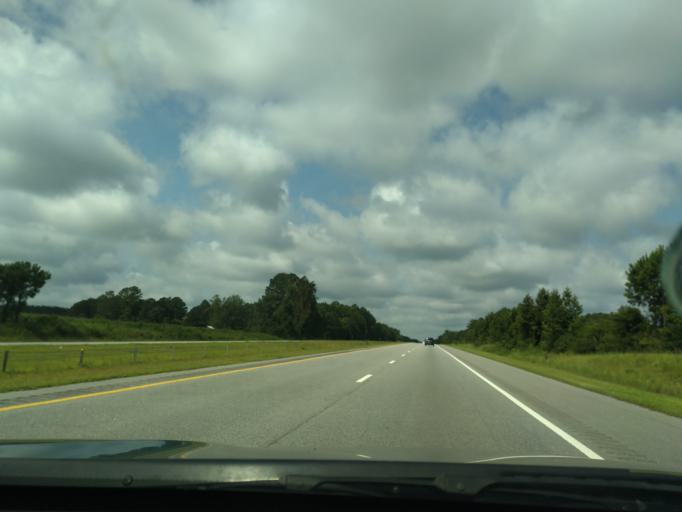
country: US
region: North Carolina
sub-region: Martin County
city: Williamston
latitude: 35.8291
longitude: -77.1259
